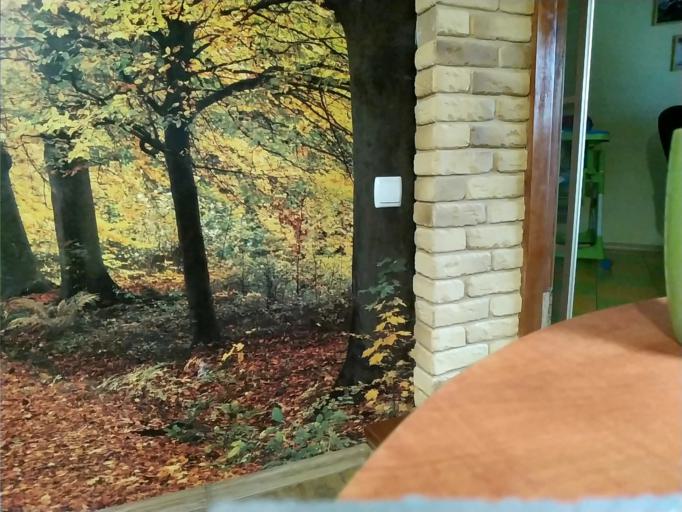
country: RU
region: Tverskaya
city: Staraya Toropa
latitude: 56.3530
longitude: 31.8064
